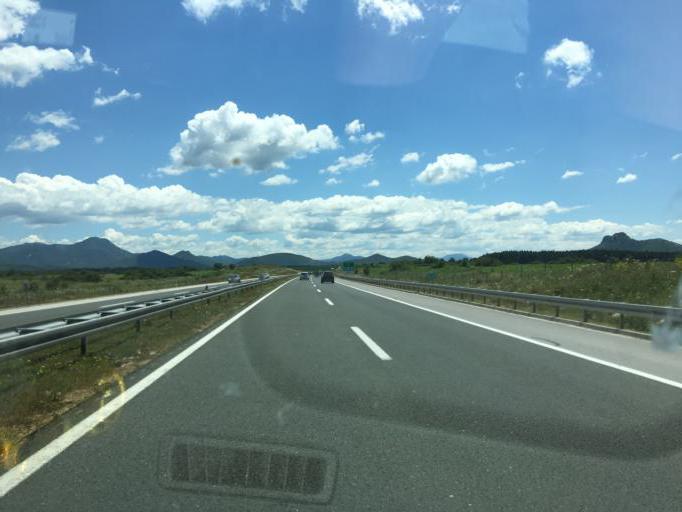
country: HR
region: Licko-Senjska
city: Gospic
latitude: 44.4717
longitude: 15.5876
